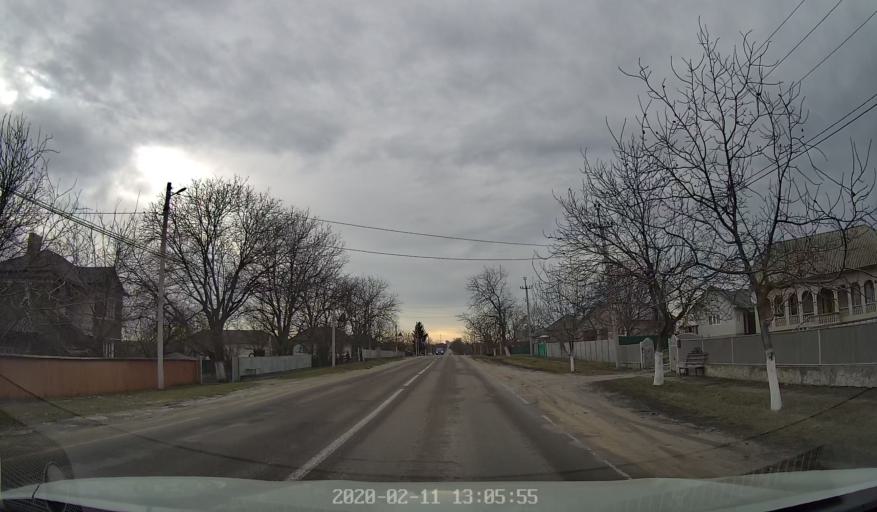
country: RO
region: Botosani
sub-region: Comuna Radauti-Prut
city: Miorcani
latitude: 48.2942
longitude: 26.9287
